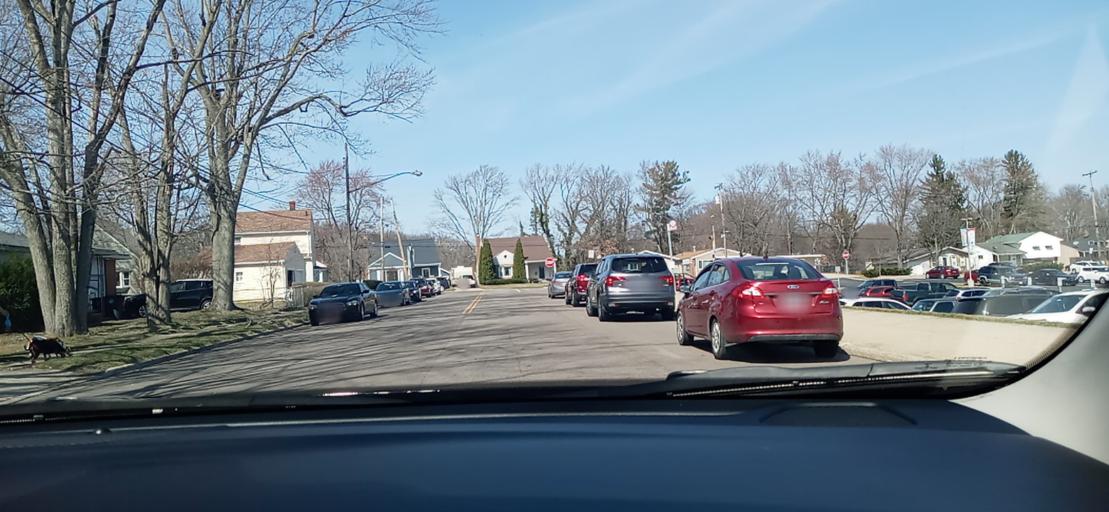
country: US
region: Ohio
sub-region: Summit County
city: Fairlawn
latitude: 41.1186
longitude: -81.5668
